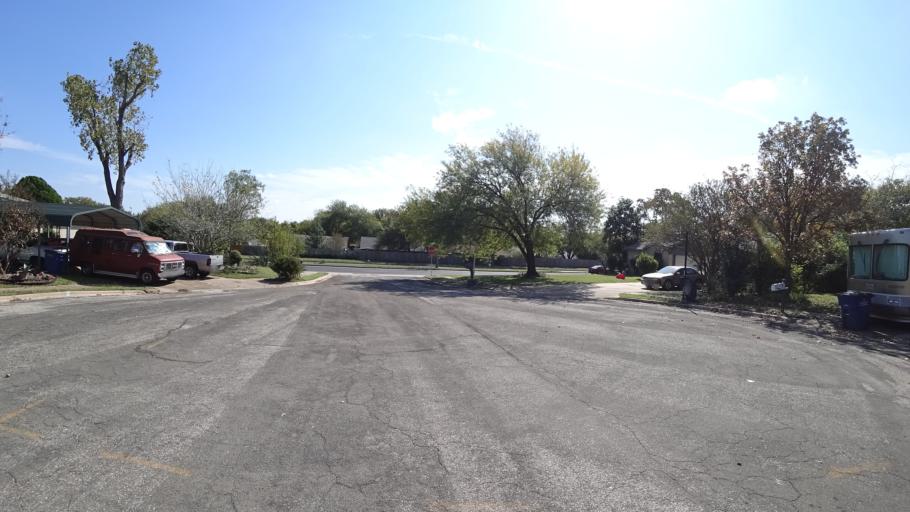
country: US
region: Texas
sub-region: Travis County
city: Rollingwood
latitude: 30.2161
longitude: -97.8139
